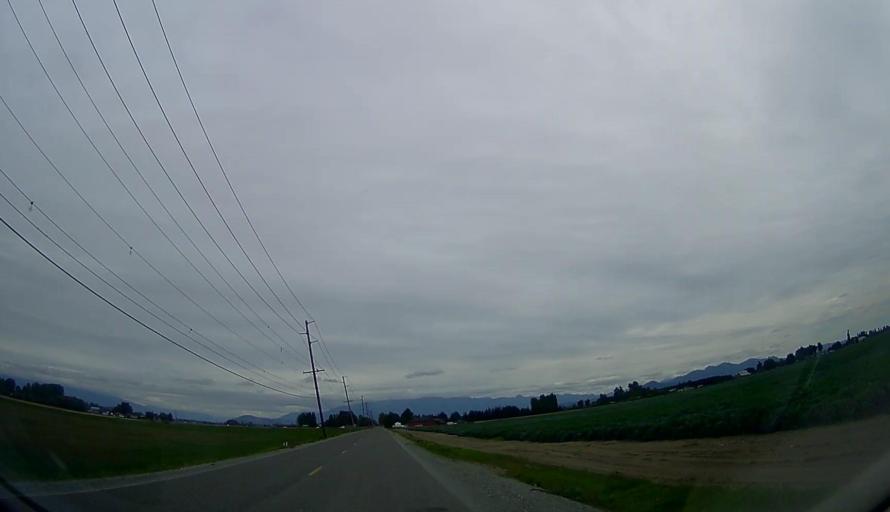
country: US
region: Washington
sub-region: Skagit County
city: Mount Vernon
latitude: 48.4426
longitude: -122.4311
